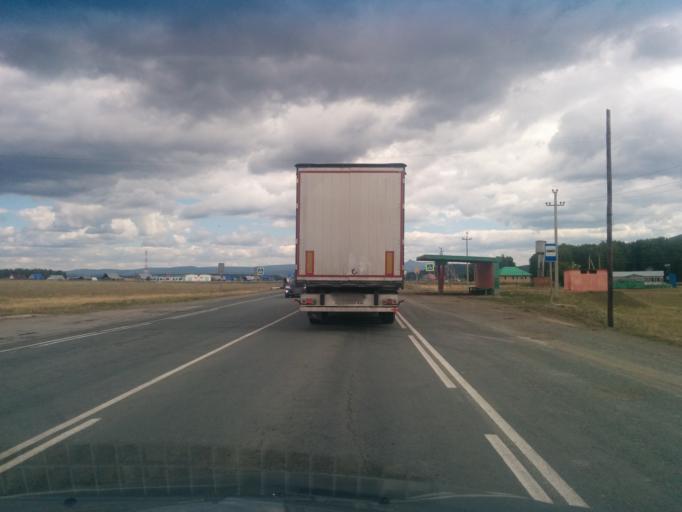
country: RU
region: Bashkortostan
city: Lomovka
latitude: 53.8814
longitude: 58.1048
